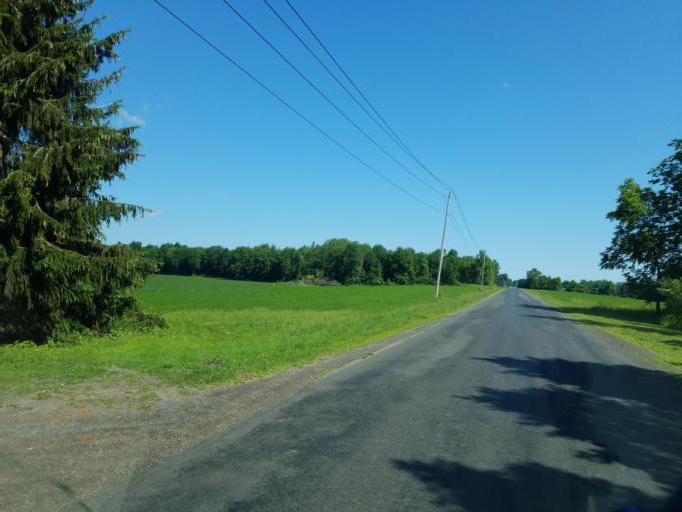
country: US
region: New York
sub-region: Wayne County
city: Wolcott
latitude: 43.1755
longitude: -76.8666
